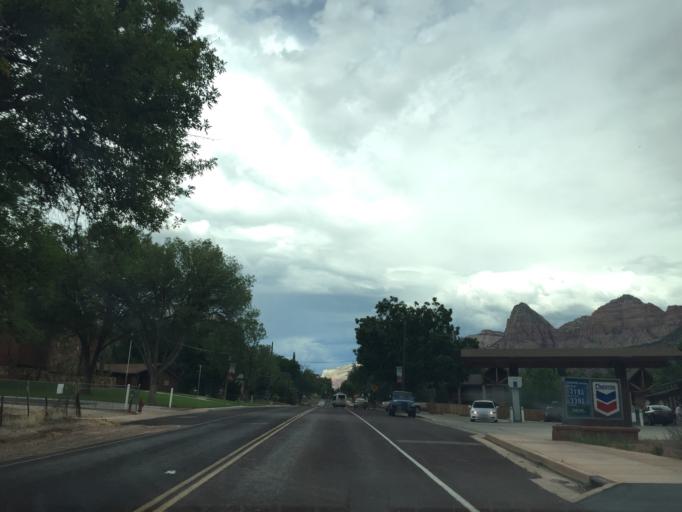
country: US
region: Utah
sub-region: Washington County
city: Hildale
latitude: 37.1785
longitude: -113.0079
